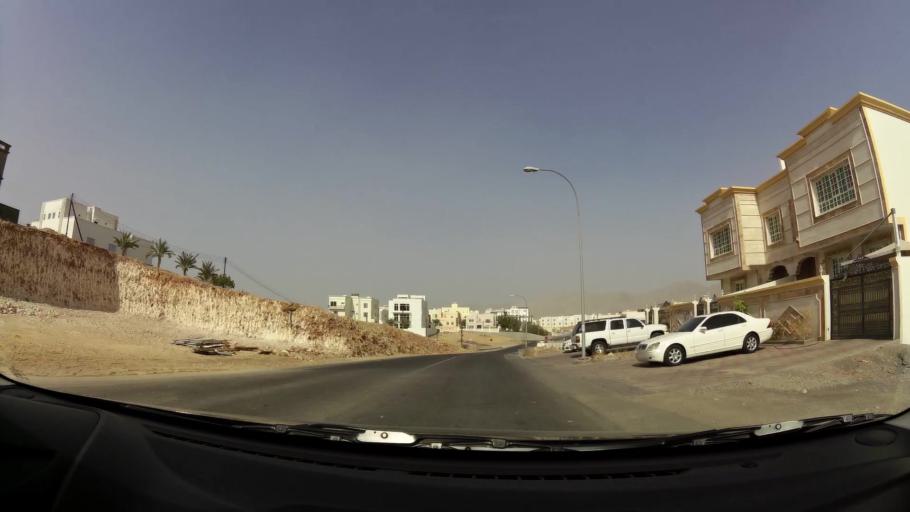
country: OM
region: Muhafazat Masqat
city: Bawshar
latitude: 23.5604
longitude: 58.3572
